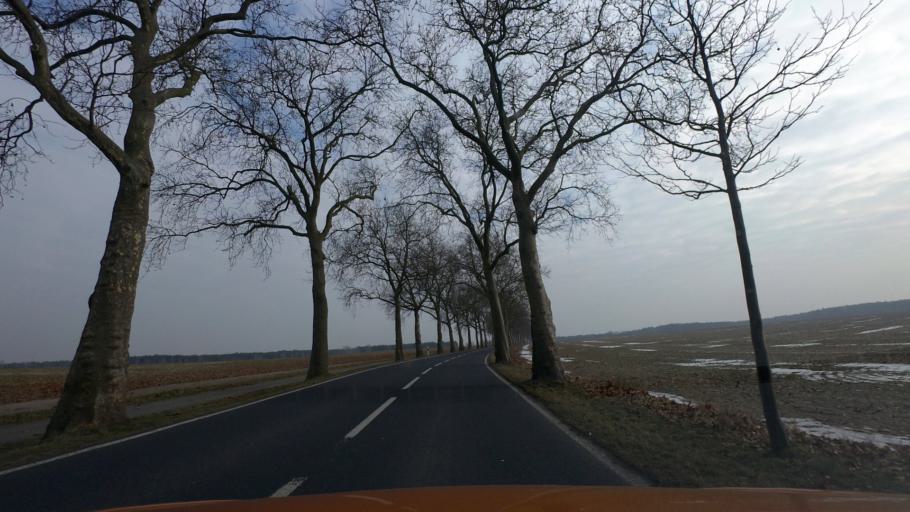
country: DE
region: Brandenburg
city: Rangsdorf
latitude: 52.2471
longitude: 13.3909
